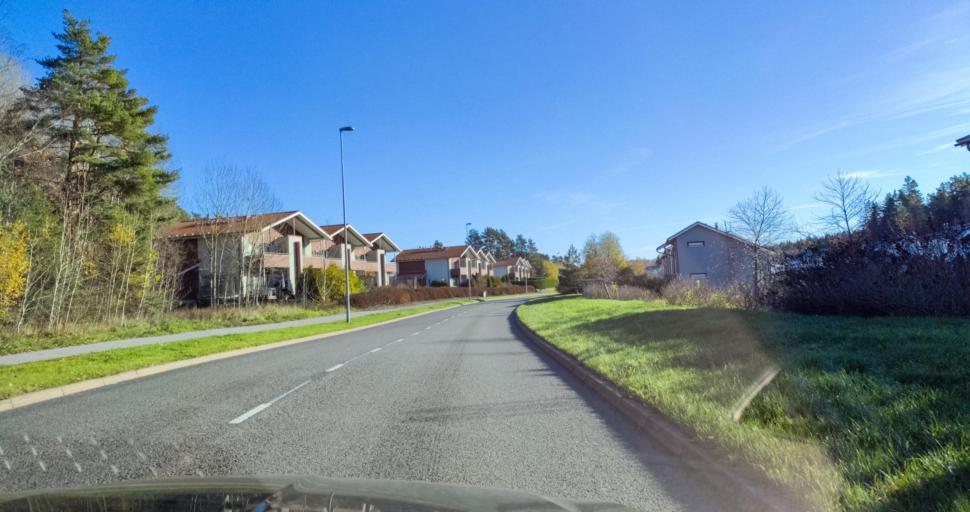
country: FI
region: Varsinais-Suomi
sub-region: Turku
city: Turku
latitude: 60.4104
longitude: 22.2141
